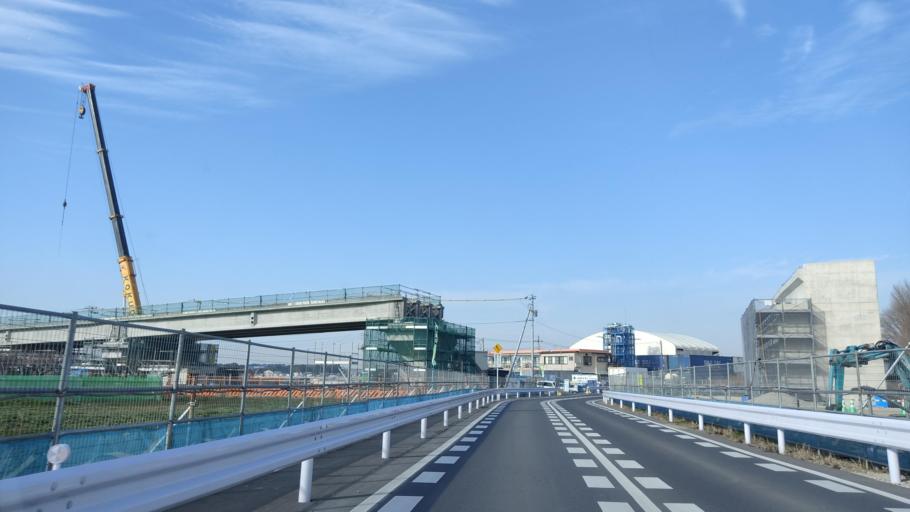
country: JP
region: Chiba
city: Nagareyama
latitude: 35.8642
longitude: 139.8951
